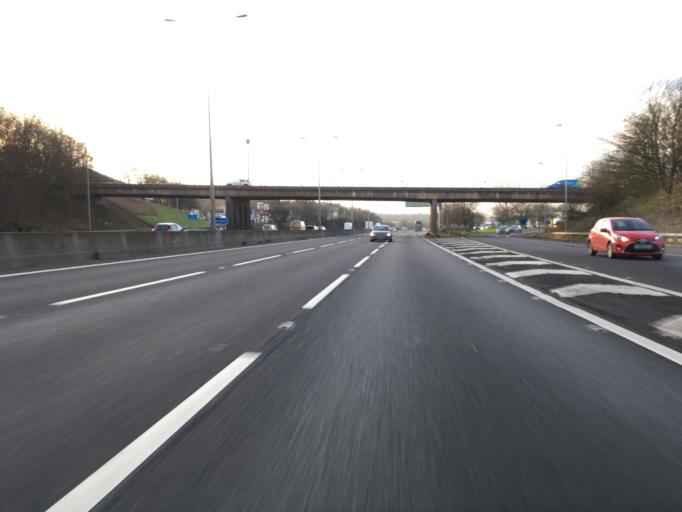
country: GB
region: England
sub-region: City and Borough of Birmingham
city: Bartley Green
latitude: 52.4313
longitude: -2.0177
